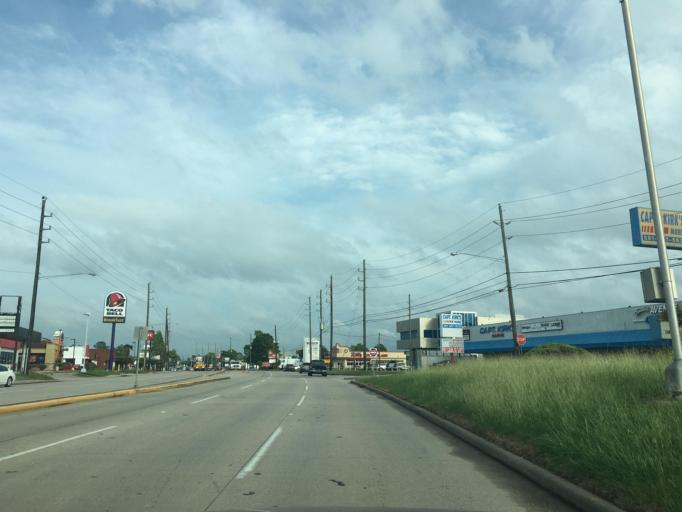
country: US
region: Texas
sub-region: Montgomery County
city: Oak Ridge North
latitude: 30.1269
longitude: -95.4538
